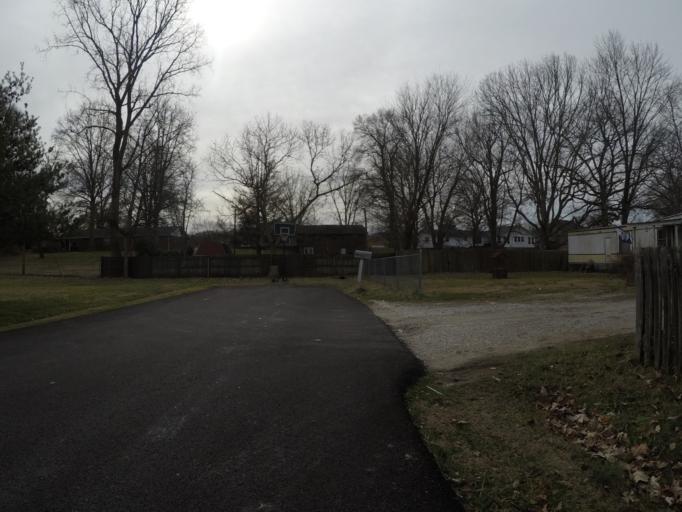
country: US
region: West Virginia
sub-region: Cabell County
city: Pea Ridge
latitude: 38.4497
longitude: -82.3431
